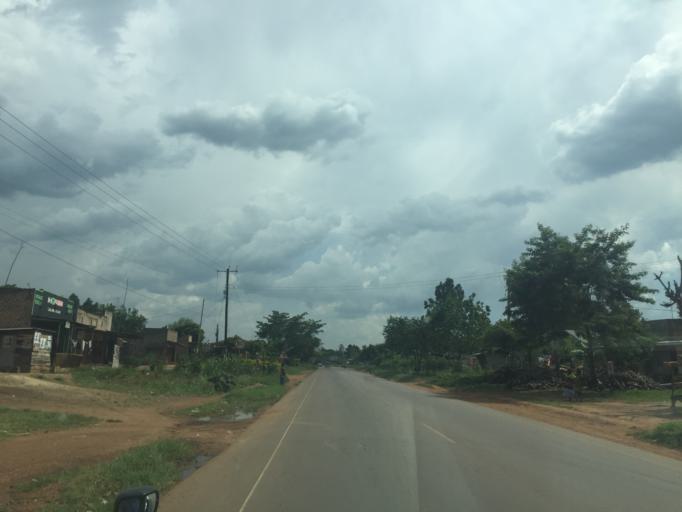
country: UG
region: Central Region
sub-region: Luwero District
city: Wobulenzi
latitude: 0.6879
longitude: 32.5229
